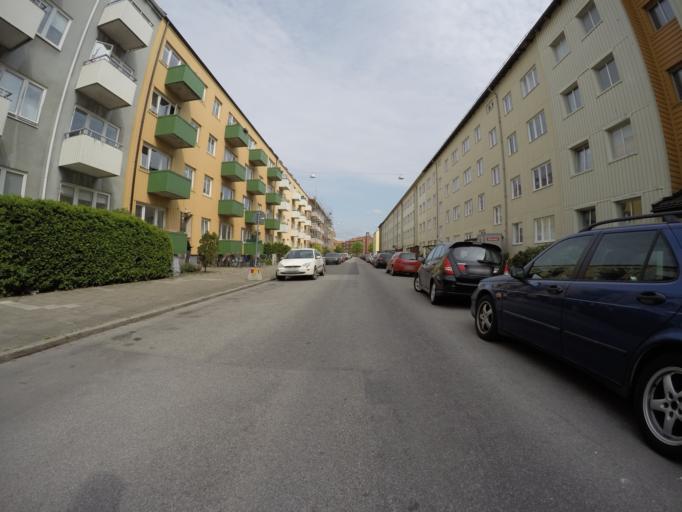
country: SE
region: Skane
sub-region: Malmo
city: Malmoe
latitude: 55.5928
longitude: 13.0243
